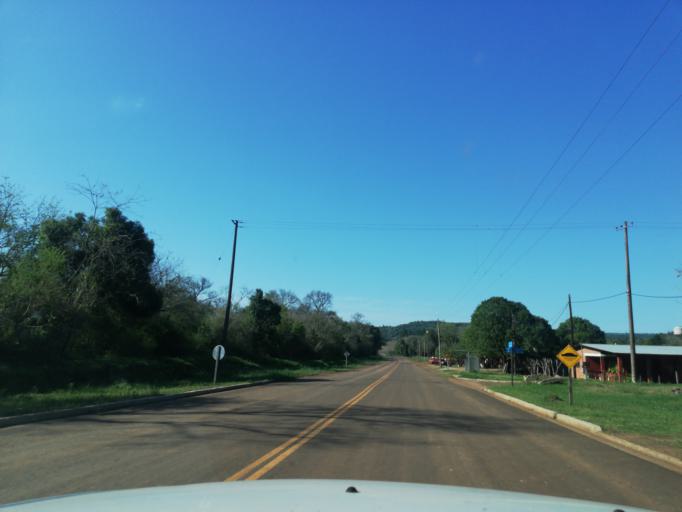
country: AR
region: Misiones
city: Arroyo del Medio
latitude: -27.6964
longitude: -55.4039
